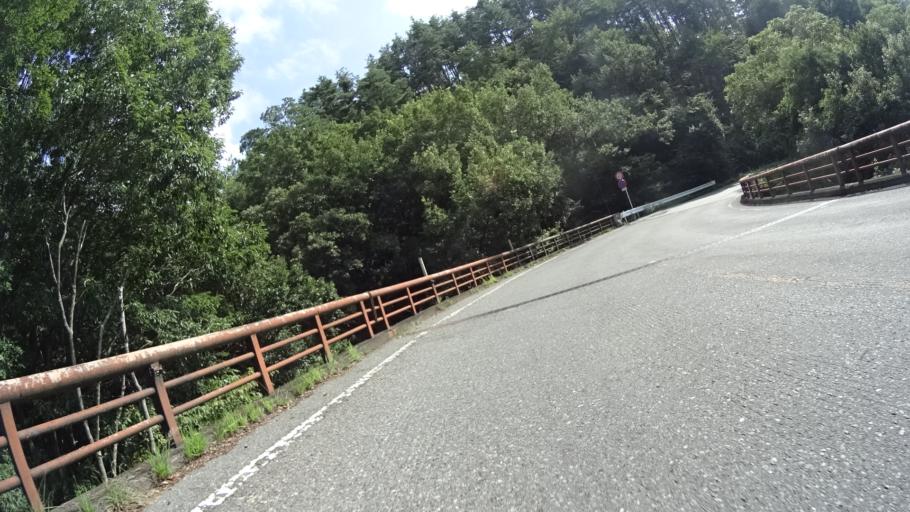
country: JP
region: Yamanashi
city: Kofu-shi
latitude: 35.7179
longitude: 138.5550
